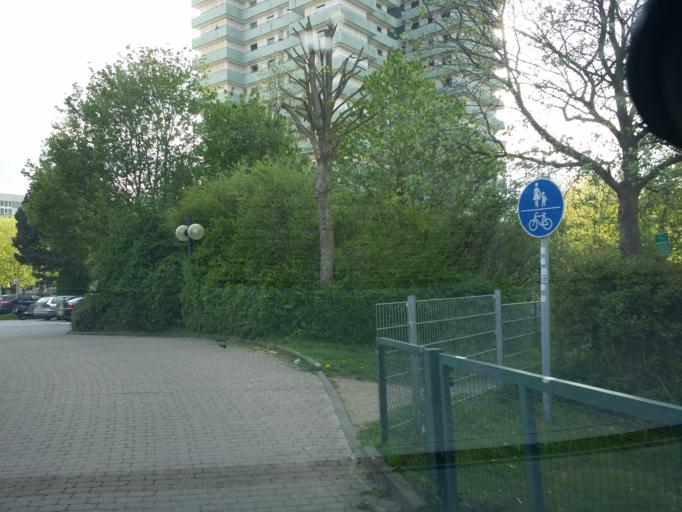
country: DE
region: Schleswig-Holstein
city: Kronshagen
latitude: 54.3455
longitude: 10.0941
